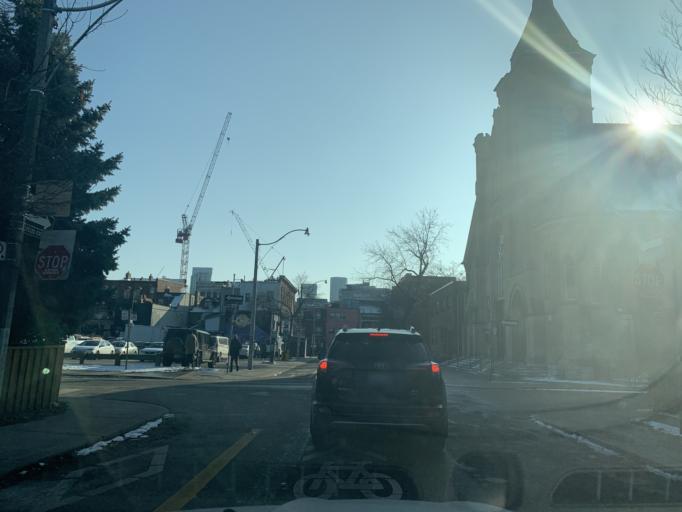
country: CA
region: Ontario
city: Toronto
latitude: 43.6489
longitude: -79.4010
